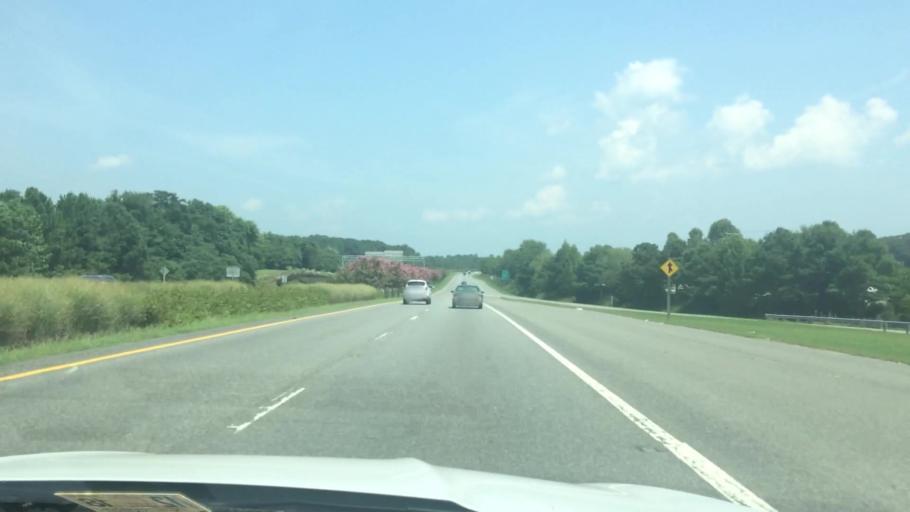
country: US
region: Virginia
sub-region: James City County
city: Williamsburg
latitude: 37.3449
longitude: -76.7420
